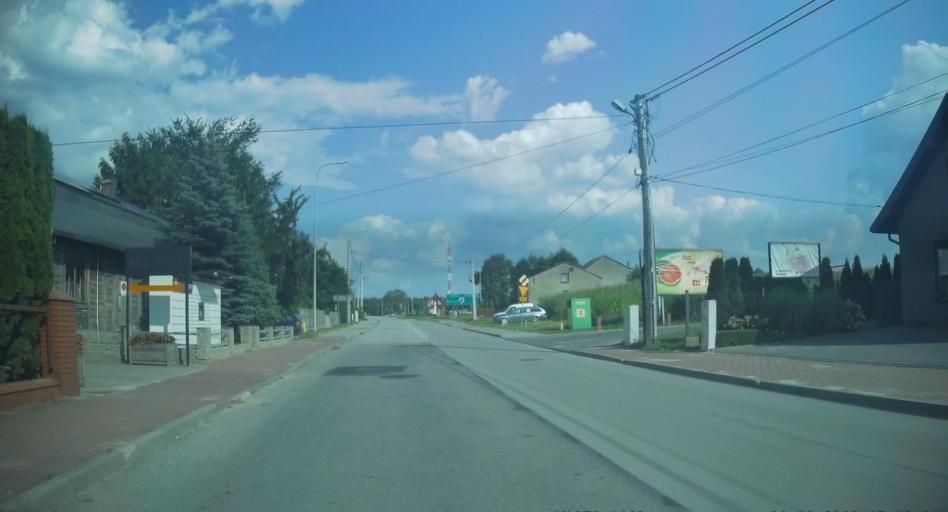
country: PL
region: Swietokrzyskie
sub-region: Powiat konecki
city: Radoszyce
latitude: 51.0721
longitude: 20.2661
